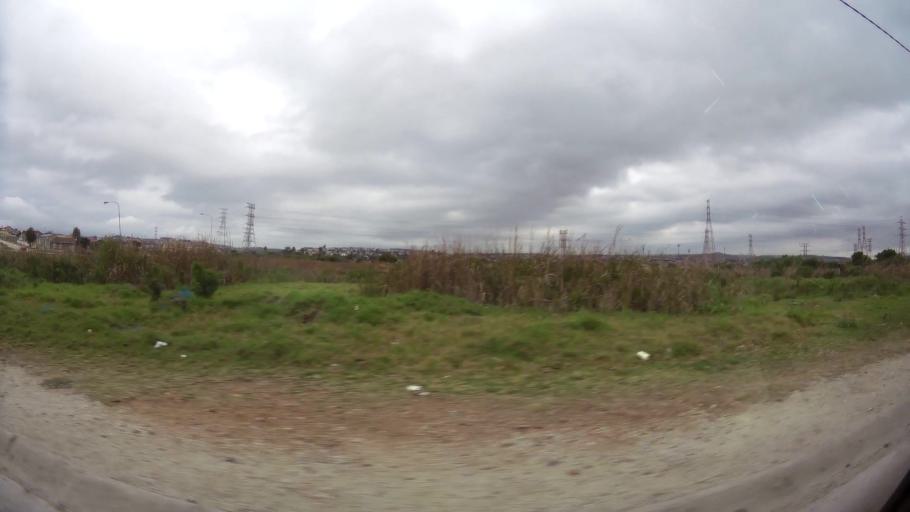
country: ZA
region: Eastern Cape
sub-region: Nelson Mandela Bay Metropolitan Municipality
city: Port Elizabeth
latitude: -33.9137
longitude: 25.5705
